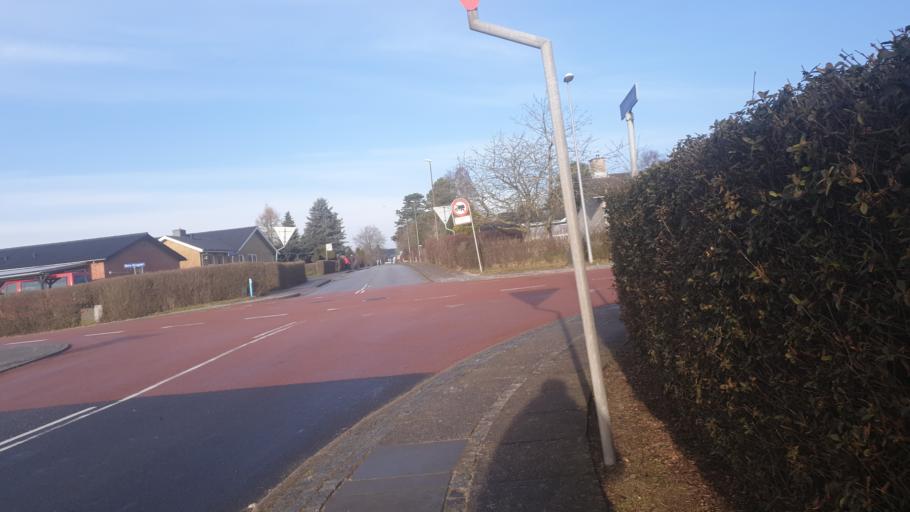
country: DK
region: Central Jutland
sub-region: Hedensted Kommune
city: Hedensted
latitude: 55.7758
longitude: 9.7159
